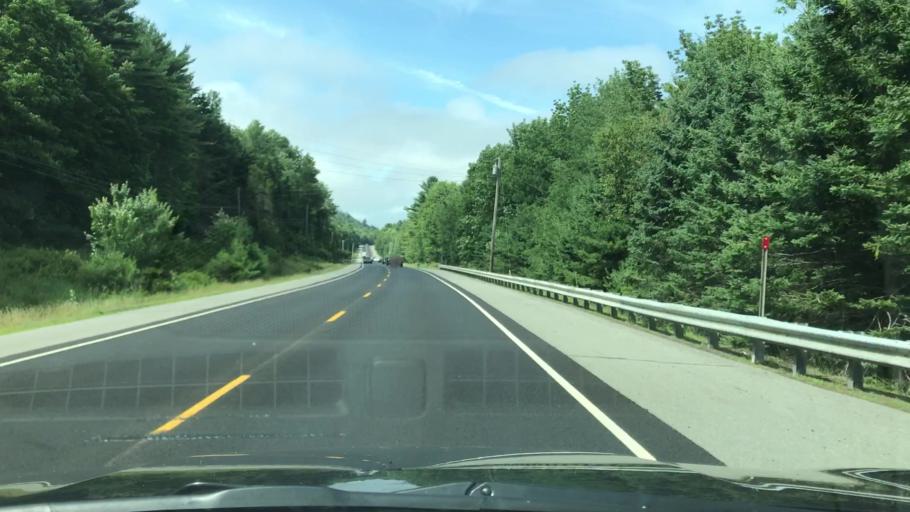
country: US
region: Maine
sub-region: Hancock County
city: Bucksport
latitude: 44.5335
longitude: -68.8086
